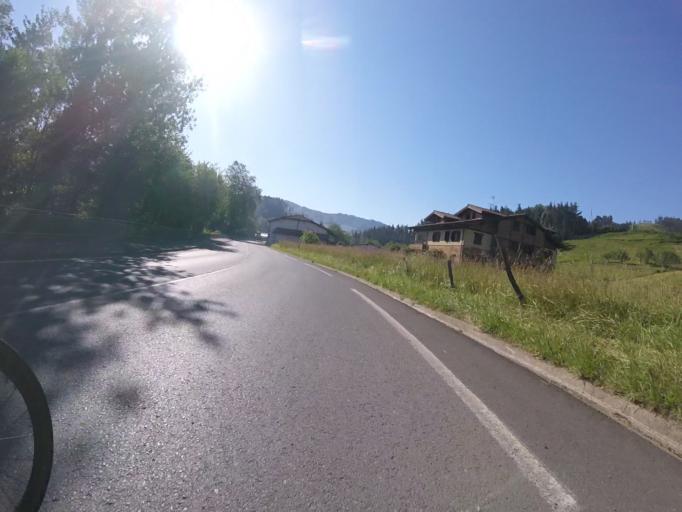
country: ES
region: Basque Country
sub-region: Provincia de Guipuzcoa
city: Azpeitia
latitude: 43.1705
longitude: -2.2548
